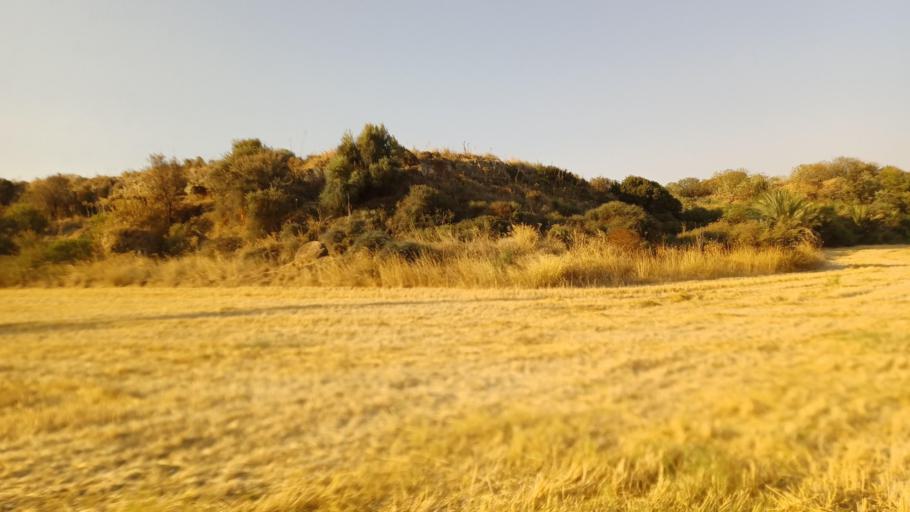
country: CY
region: Pafos
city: Polis
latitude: 35.0583
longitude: 32.4598
